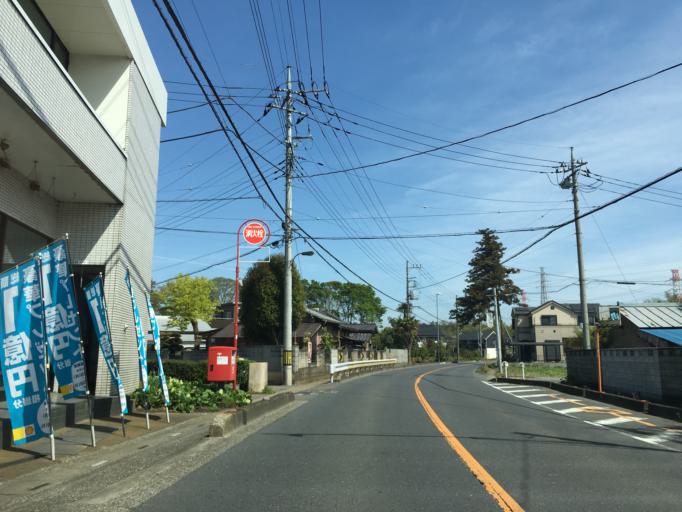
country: JP
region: Saitama
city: Shiraoka
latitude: 35.9998
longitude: 139.6953
